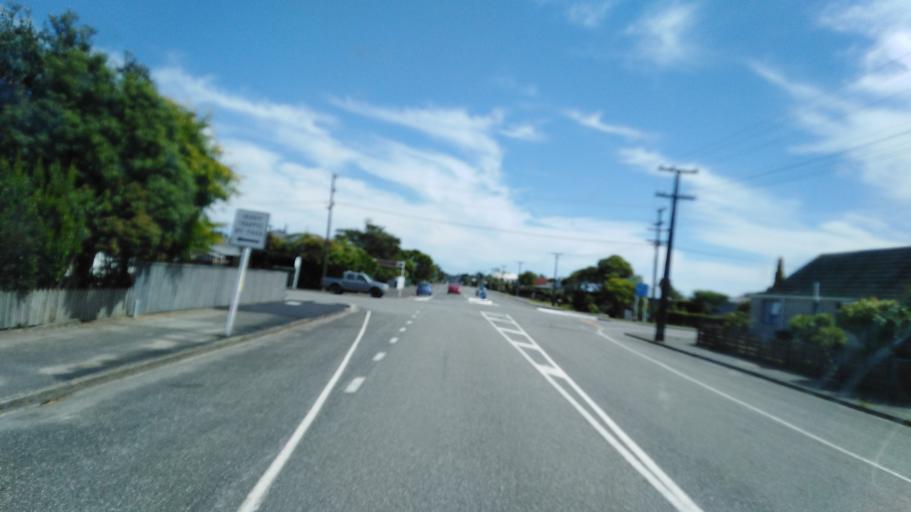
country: NZ
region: West Coast
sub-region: Buller District
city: Westport
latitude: -41.7538
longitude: 171.6115
